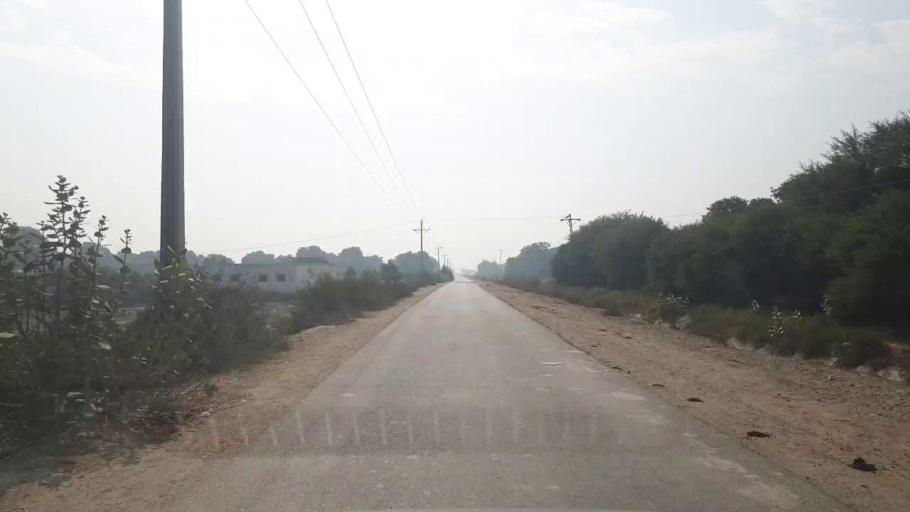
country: PK
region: Sindh
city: Hala
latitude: 25.7938
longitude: 68.4394
